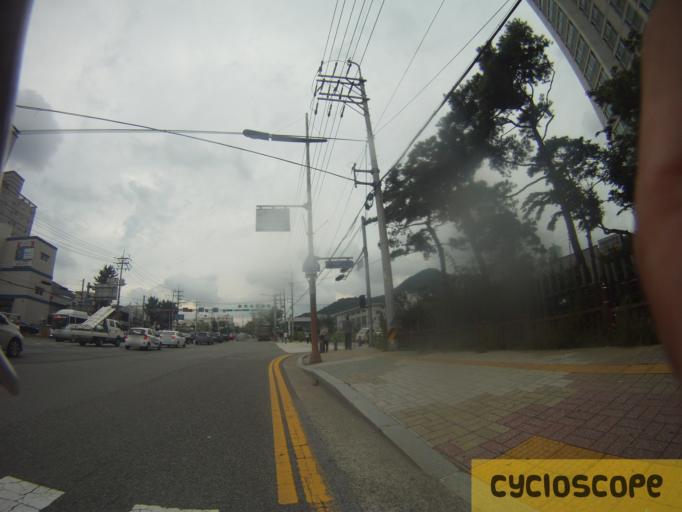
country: KR
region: Busan
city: Busan
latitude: 35.1730
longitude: 129.1032
